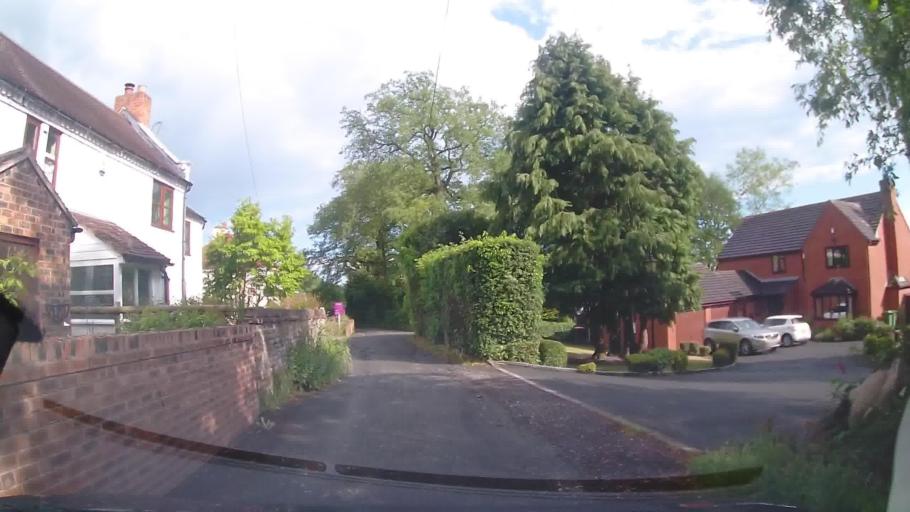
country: GB
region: England
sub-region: Telford and Wrekin
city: Ironbridge
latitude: 52.6438
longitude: -2.4997
